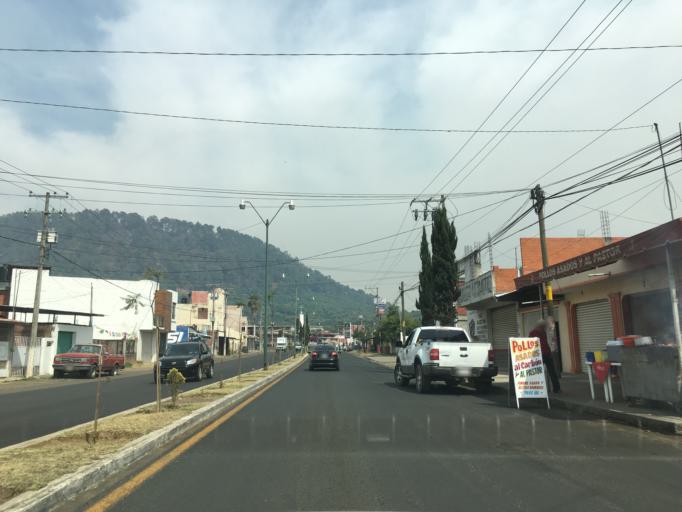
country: MX
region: Michoacan
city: Nuevo San Juan Parangaricutiro
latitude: 19.4133
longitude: -102.1180
